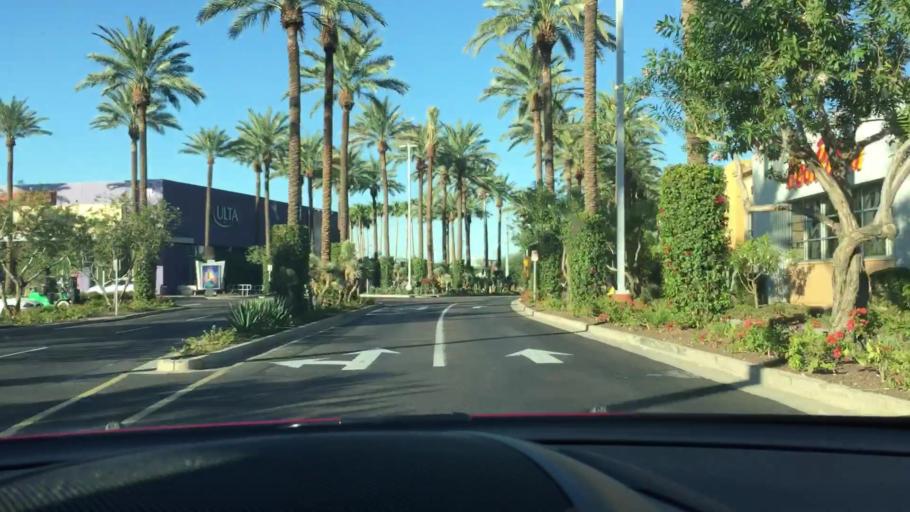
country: US
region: Arizona
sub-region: Maricopa County
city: Tempe
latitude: 33.4323
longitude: -111.9074
